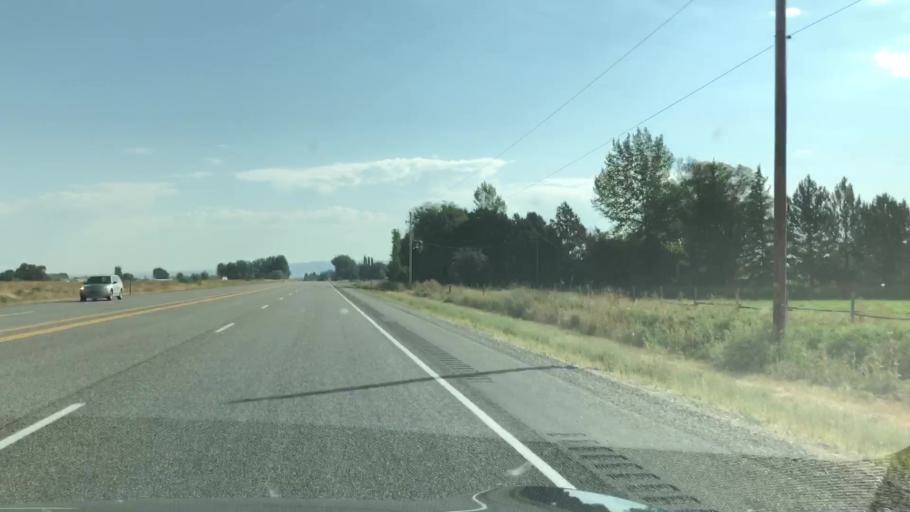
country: US
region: Idaho
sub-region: Jefferson County
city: Rigby
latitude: 43.5986
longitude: -111.8601
